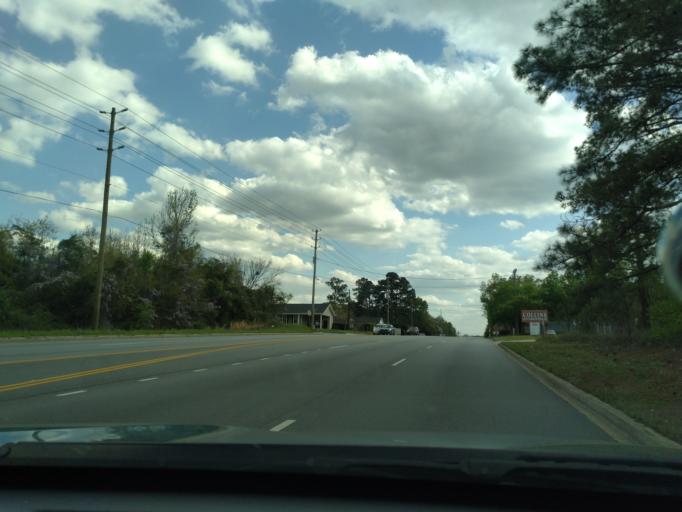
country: US
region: South Carolina
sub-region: Florence County
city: Florence
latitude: 34.1702
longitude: -79.7606
